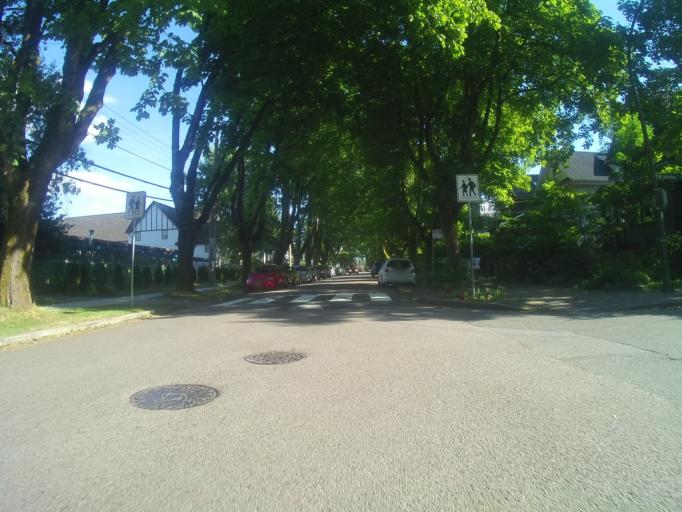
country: CA
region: British Columbia
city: Vancouver
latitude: 49.2588
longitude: -123.1201
